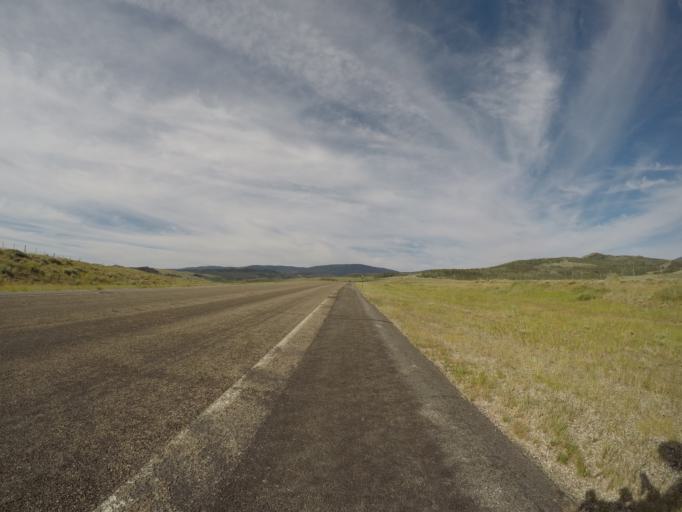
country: US
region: Wyoming
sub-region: Carbon County
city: Saratoga
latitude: 41.1906
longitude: -106.8528
